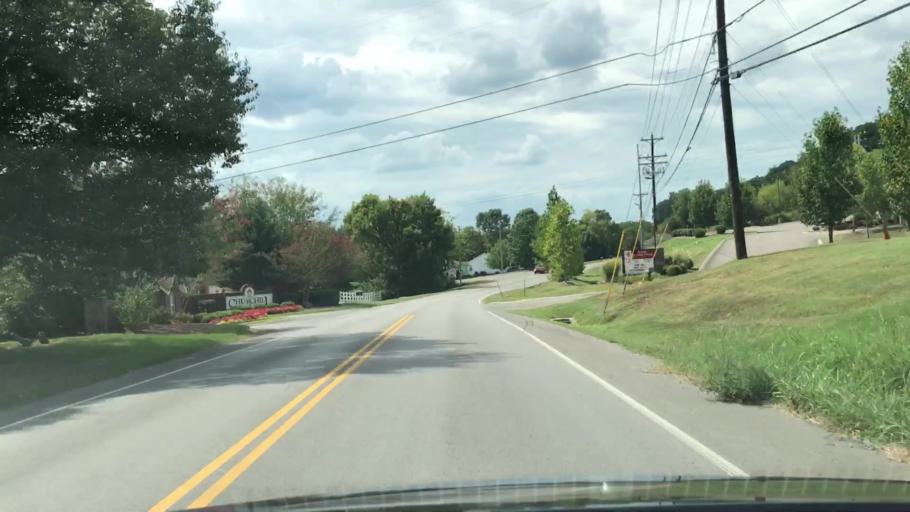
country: US
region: Tennessee
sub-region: Williamson County
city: Thompson's Station
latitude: 35.7828
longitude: -86.9031
